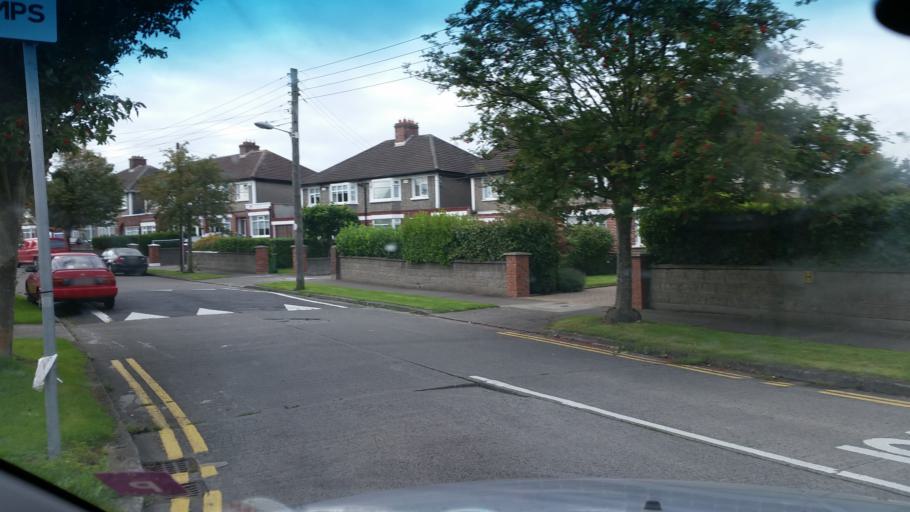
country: IE
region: Leinster
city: Ballymun
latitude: 53.3889
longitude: -6.2716
